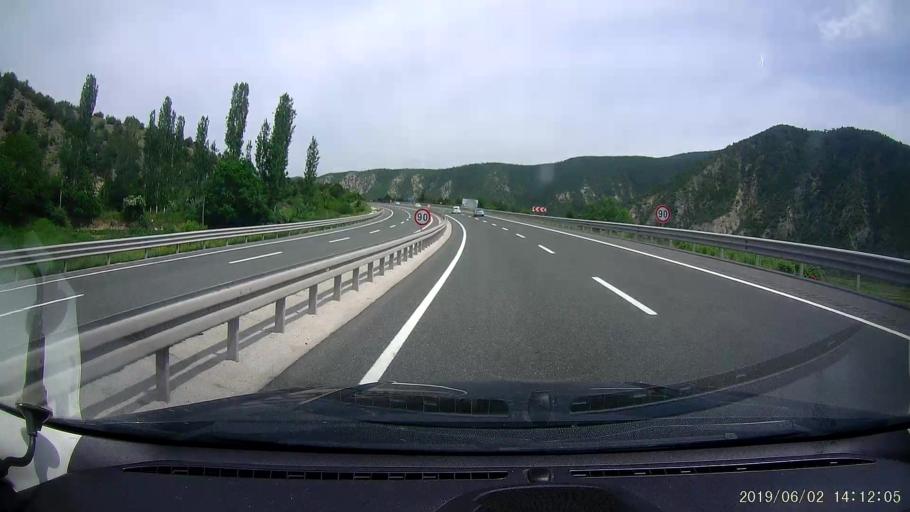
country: TR
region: Cankiri
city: Yaprakli
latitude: 40.9113
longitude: 33.8015
